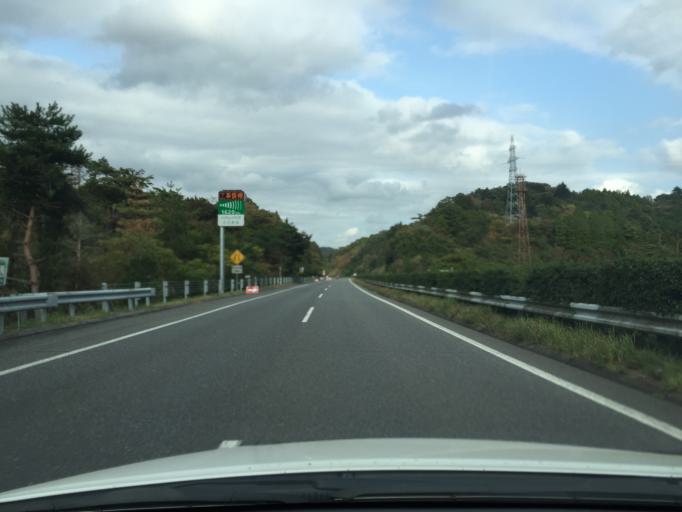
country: JP
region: Fukushima
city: Iwaki
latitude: 36.9672
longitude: 140.7872
